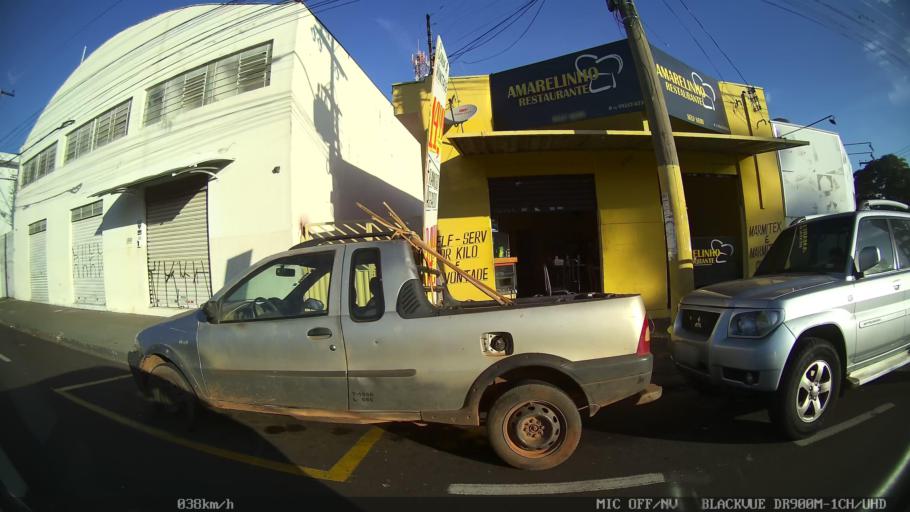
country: BR
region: Sao Paulo
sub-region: Franca
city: Franca
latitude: -20.5263
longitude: -47.3761
